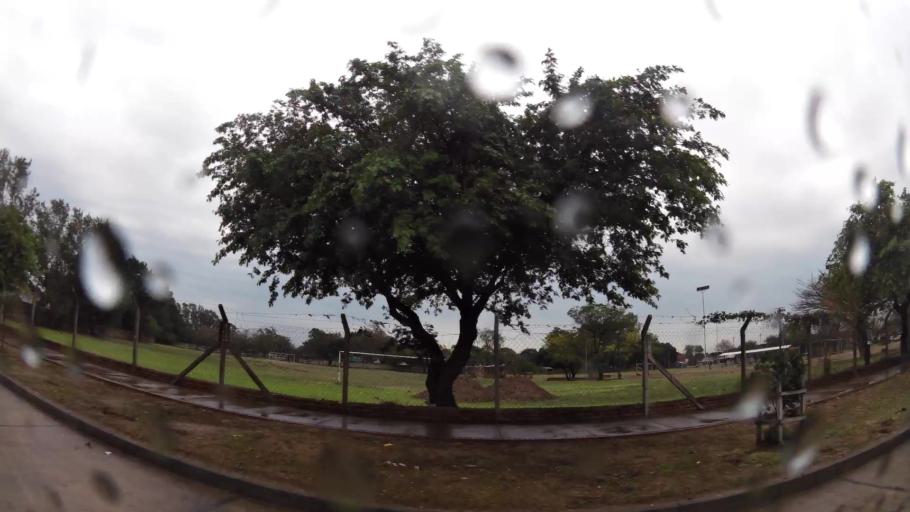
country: BO
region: Santa Cruz
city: Santa Cruz de la Sierra
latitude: -17.8110
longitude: -63.1955
